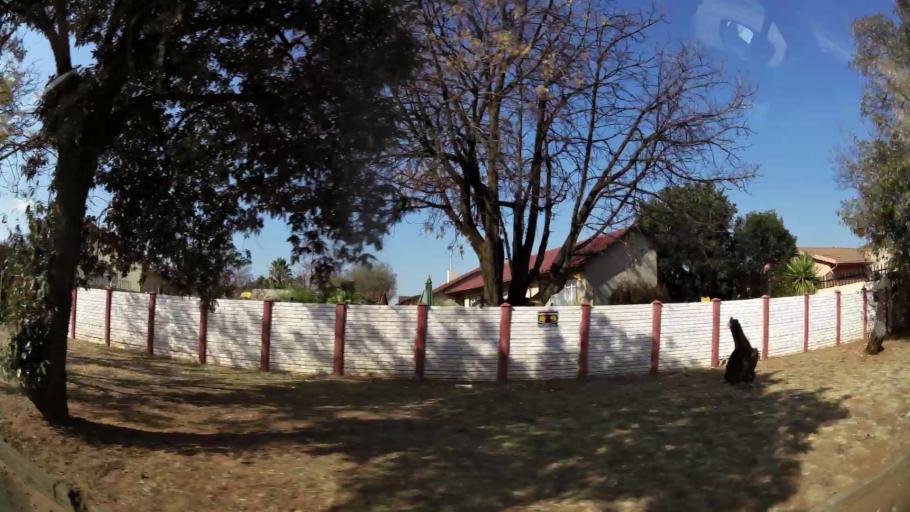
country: ZA
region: Gauteng
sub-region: West Rand District Municipality
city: Randfontein
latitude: -26.1630
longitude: 27.6988
